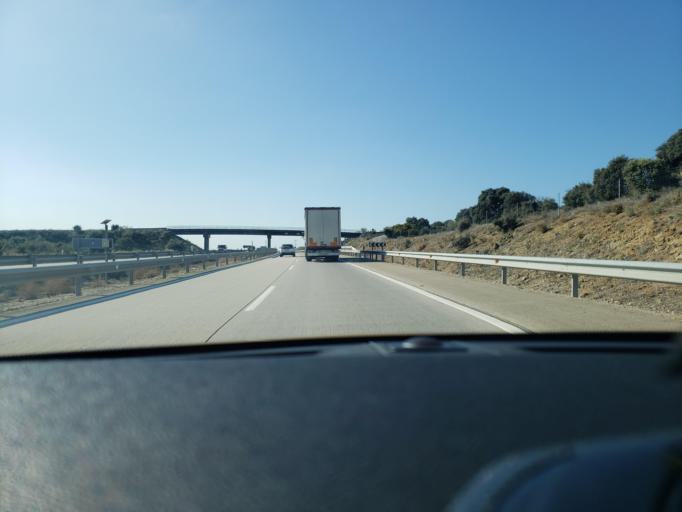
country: ES
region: Castille-La Mancha
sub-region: Province of Toledo
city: Cervera de los Montes
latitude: 40.0180
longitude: -4.8024
